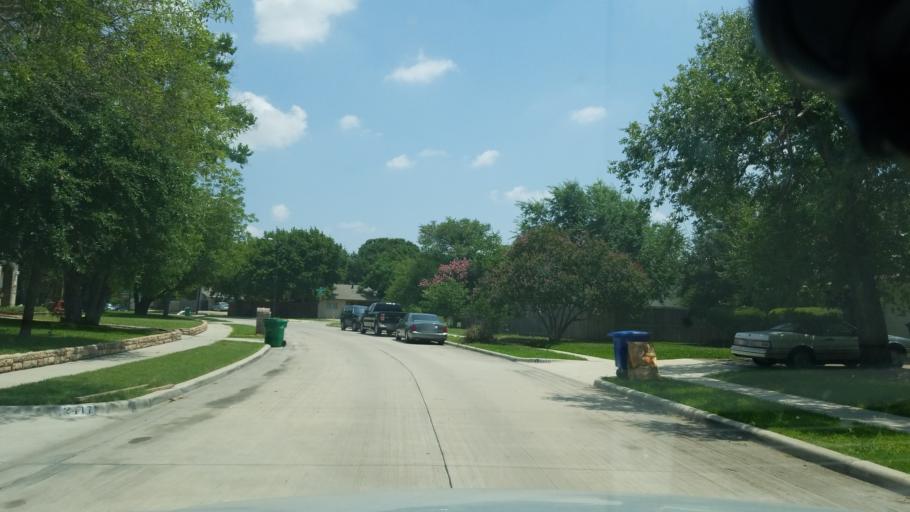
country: US
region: Texas
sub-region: Dallas County
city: Carrollton
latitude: 32.9508
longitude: -96.8726
